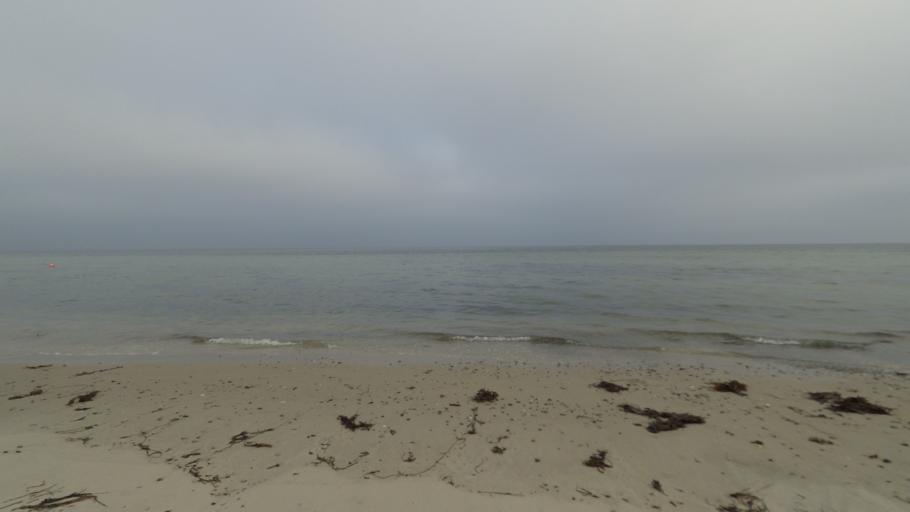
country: DK
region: Central Jutland
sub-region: Arhus Kommune
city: Malling
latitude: 55.9600
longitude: 10.2661
